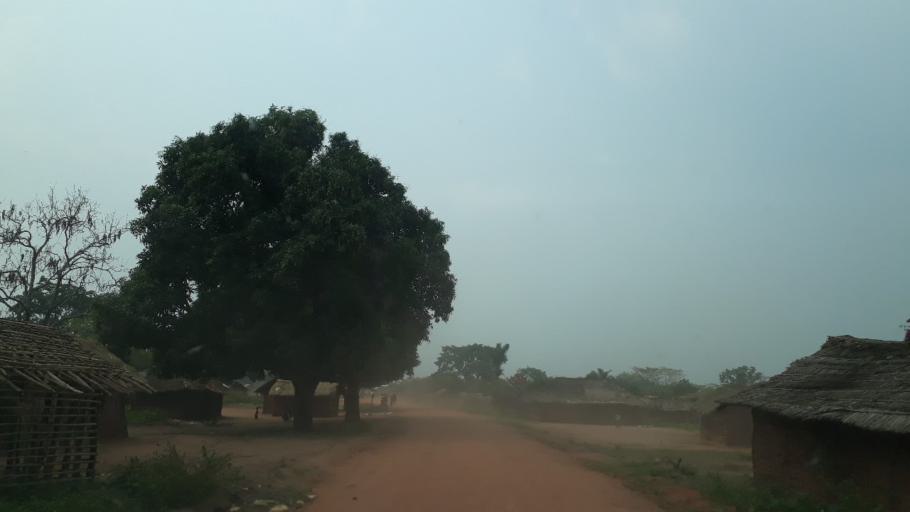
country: CD
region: Kasai-Occidental
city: Tshikapa
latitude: -6.4675
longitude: 20.4636
